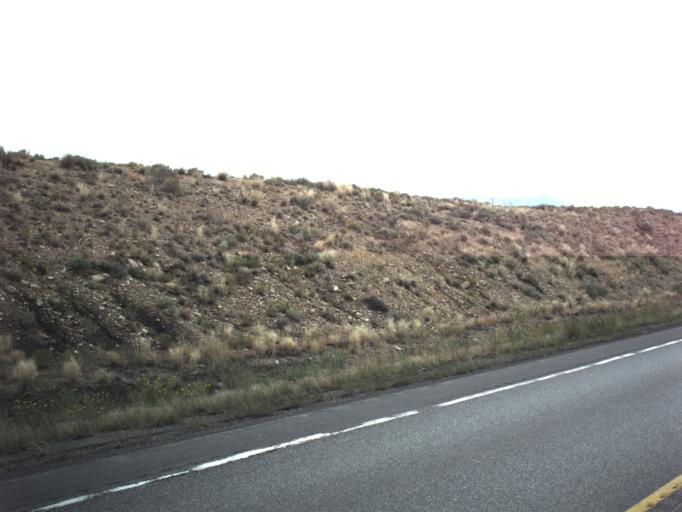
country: US
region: Utah
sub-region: Carbon County
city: East Carbon City
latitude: 39.5173
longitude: -110.5538
